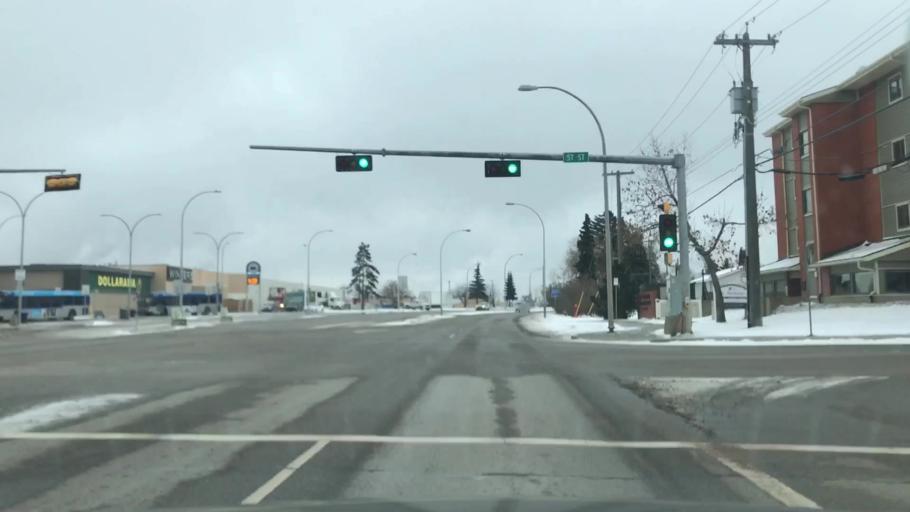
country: CA
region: Alberta
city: Edmonton
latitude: 53.5383
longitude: -113.4239
